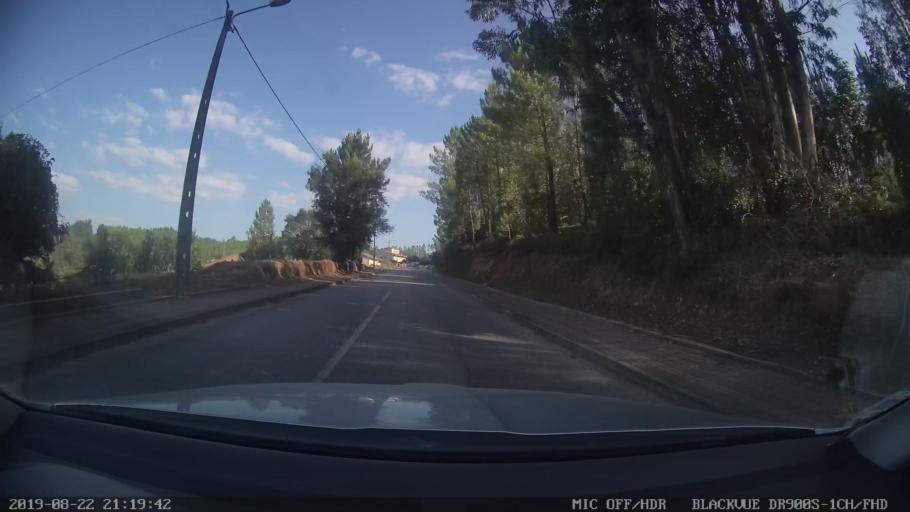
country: PT
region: Castelo Branco
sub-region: Serta
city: Serta
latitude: 39.8078
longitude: -8.1079
